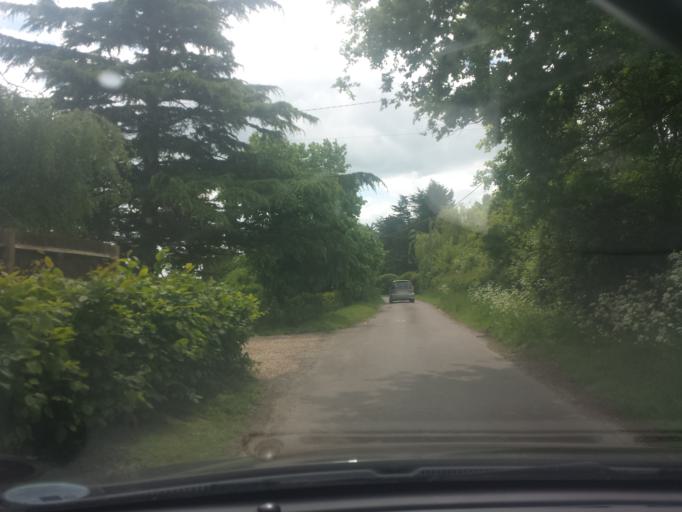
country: GB
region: England
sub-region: Essex
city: Little Clacton
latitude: 51.8685
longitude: 1.1387
